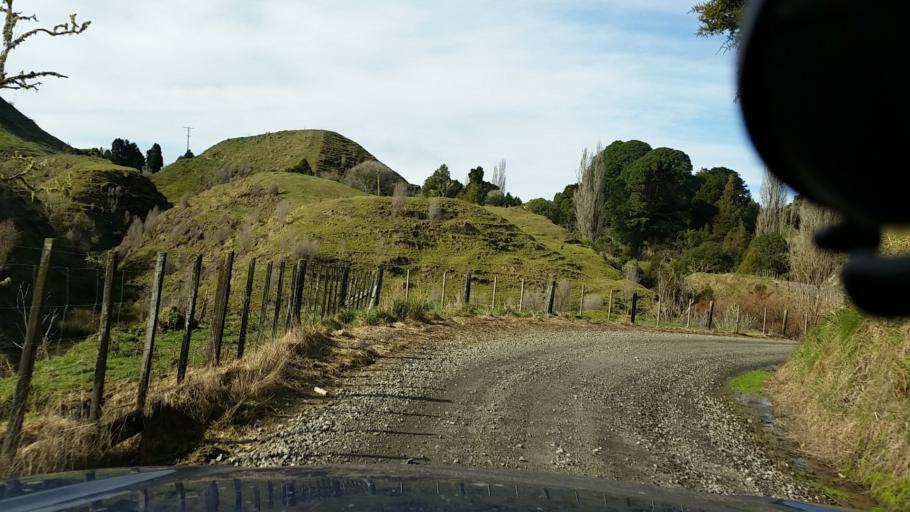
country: NZ
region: Taranaki
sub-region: New Plymouth District
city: Waitara
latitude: -39.0332
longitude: 174.7780
